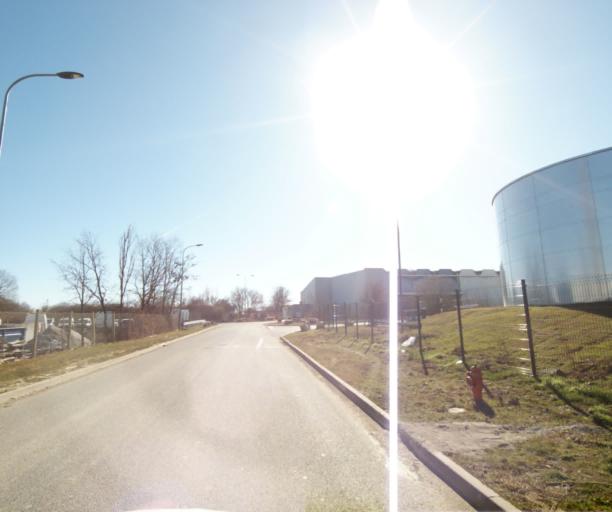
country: FR
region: Lorraine
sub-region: Departement de Meurthe-et-Moselle
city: Fleville-devant-Nancy
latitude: 48.6111
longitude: 6.1983
